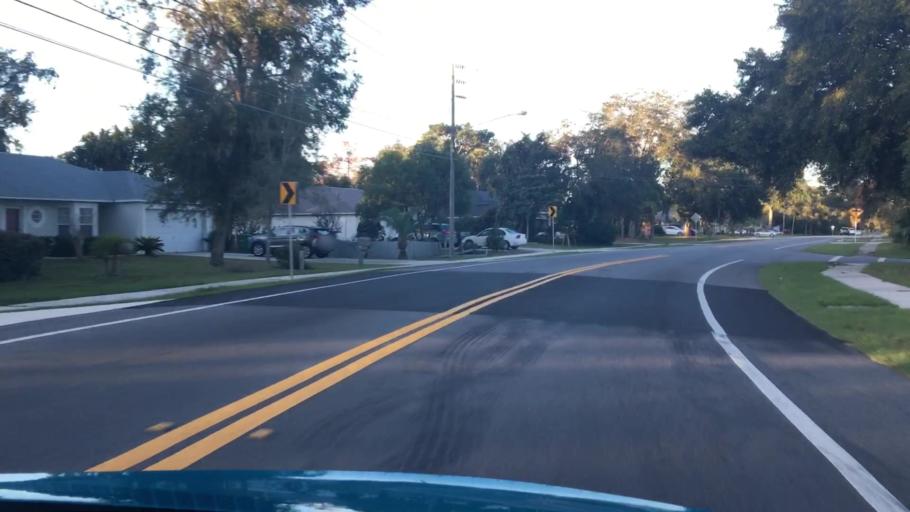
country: US
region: Florida
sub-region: Volusia County
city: Deltona
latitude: 28.8704
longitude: -81.2444
